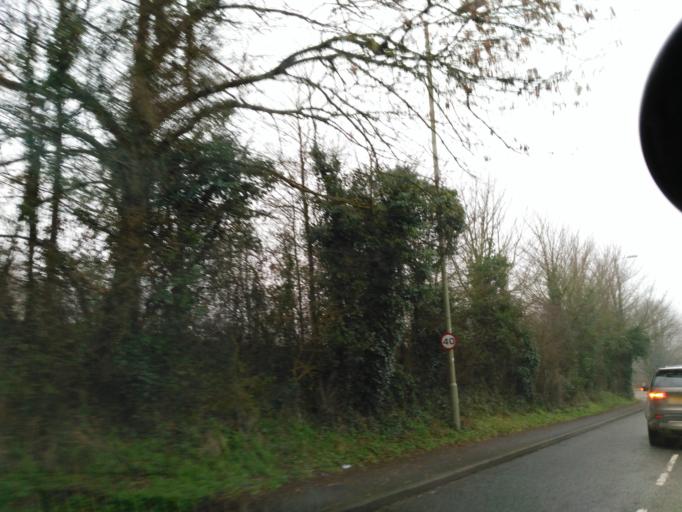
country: GB
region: England
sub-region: Hampshire
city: Lee-on-the-Solent
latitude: 50.8349
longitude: -1.2203
